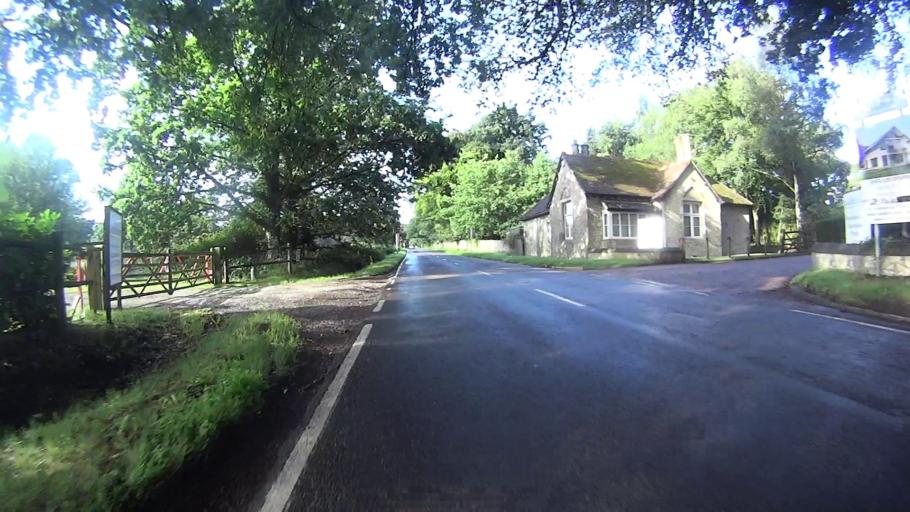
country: GB
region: England
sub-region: Surrey
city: Lingfield
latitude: 51.1611
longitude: -0.0219
